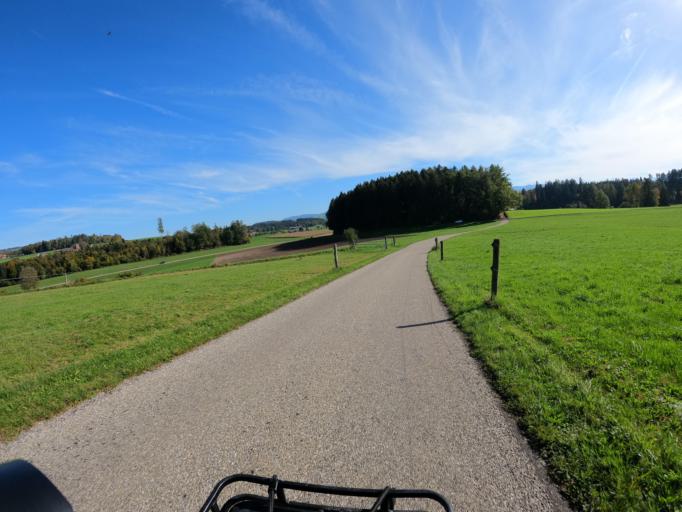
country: CH
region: Zug
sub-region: Zug
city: Steinhausen
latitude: 47.2178
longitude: 8.4992
